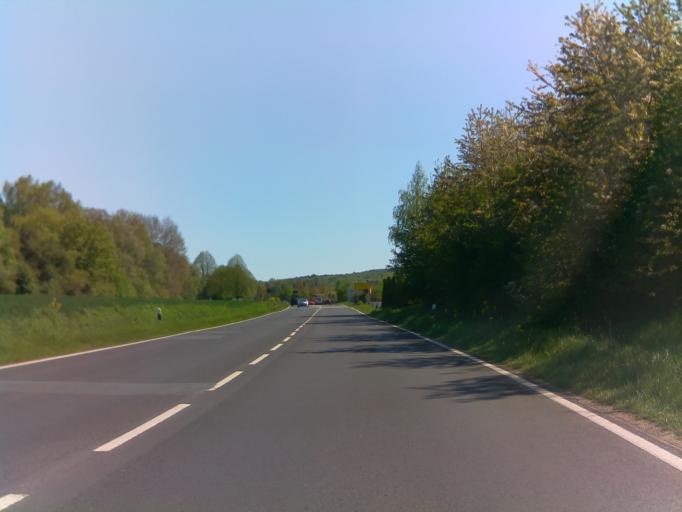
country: DE
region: Hesse
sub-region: Regierungsbezirk Giessen
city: Alsfeld
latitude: 50.7383
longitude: 9.2813
